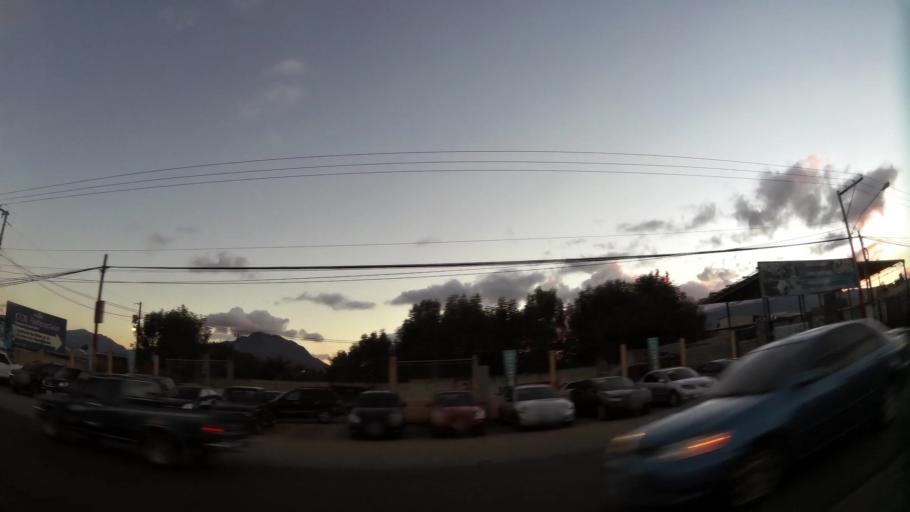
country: GT
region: Quetzaltenango
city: Olintepeque
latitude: 14.8621
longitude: -91.5286
